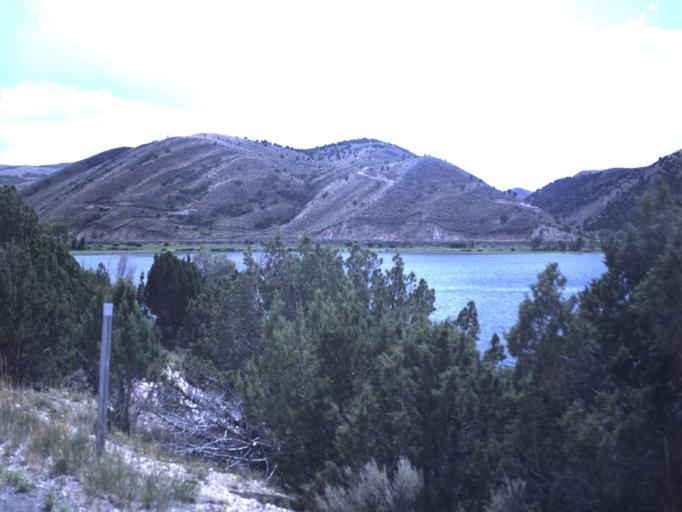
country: US
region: Utah
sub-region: Summit County
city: Oakley
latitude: 40.7617
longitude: -111.3776
